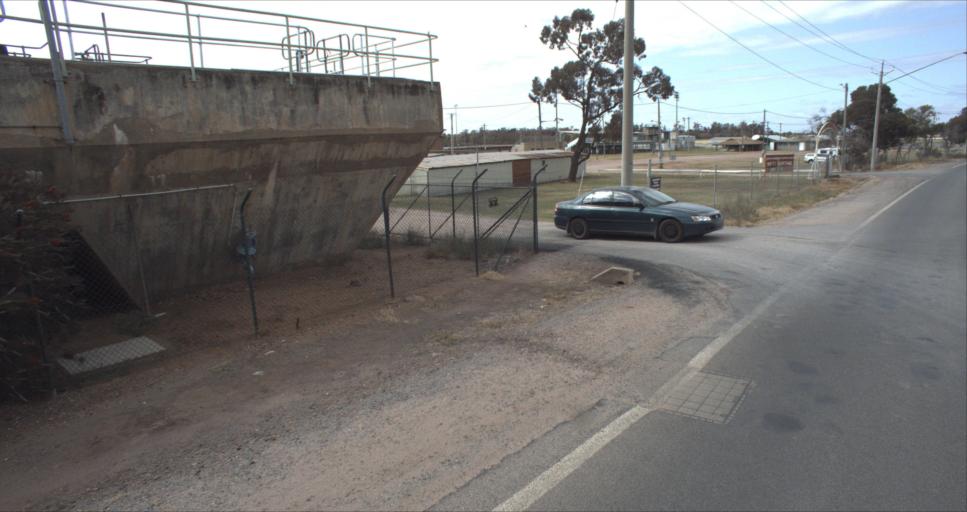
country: AU
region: New South Wales
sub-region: Leeton
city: Leeton
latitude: -34.5586
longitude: 146.4028
